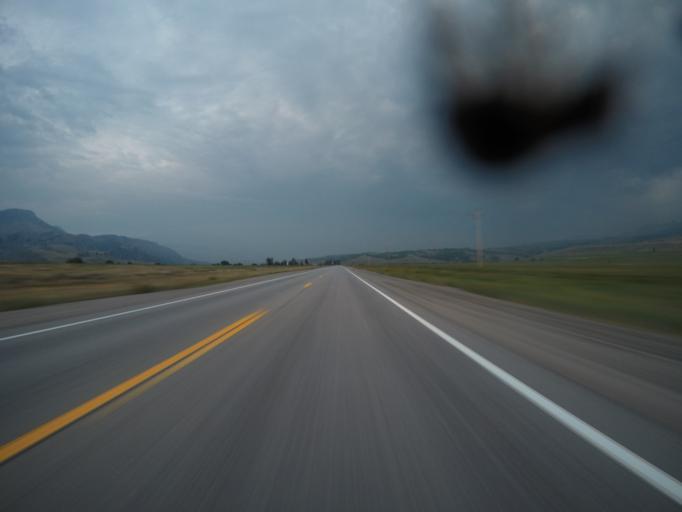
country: US
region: Colorado
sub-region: Summit County
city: Silverthorne
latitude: 39.8124
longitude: -106.1960
